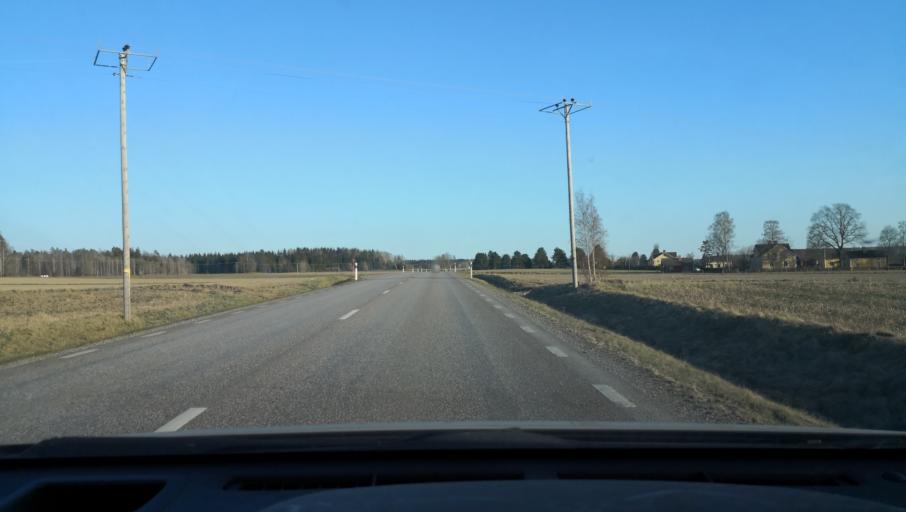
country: SE
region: Uppsala
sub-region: Heby Kommun
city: Heby
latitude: 59.9309
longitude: 16.8730
